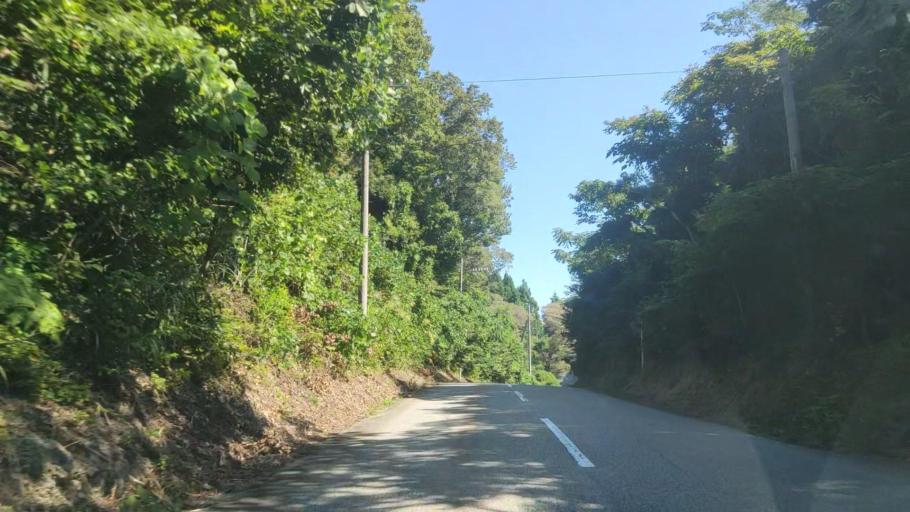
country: JP
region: Ishikawa
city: Nanao
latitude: 37.5149
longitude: 137.3327
